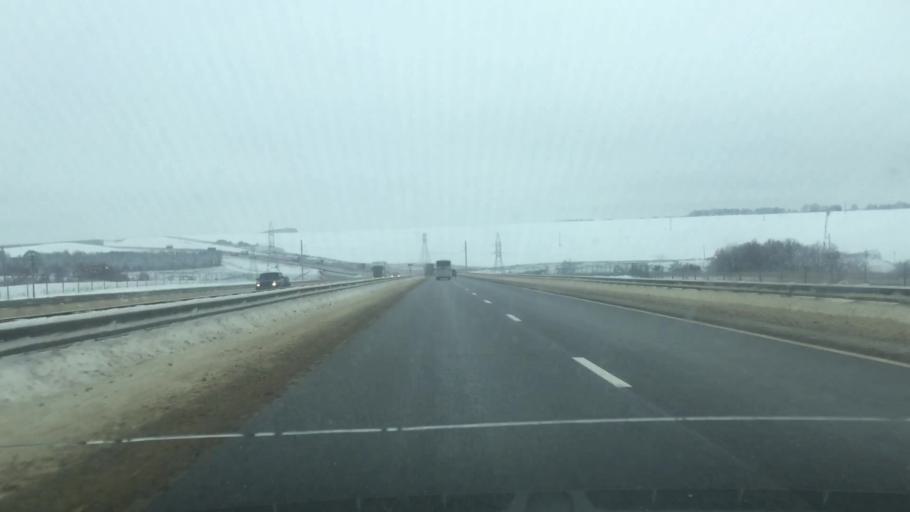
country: RU
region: Tula
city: Kazachka
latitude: 53.2807
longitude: 38.1796
